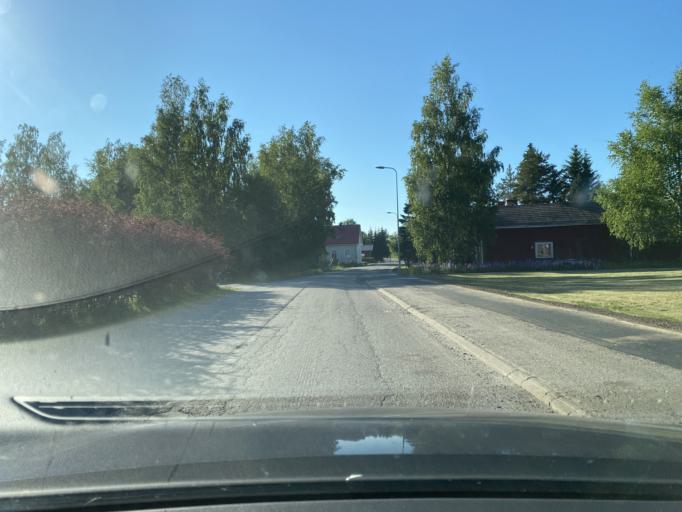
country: FI
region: Satakunta
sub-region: Pori
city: Huittinen
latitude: 61.1701
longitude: 22.6998
